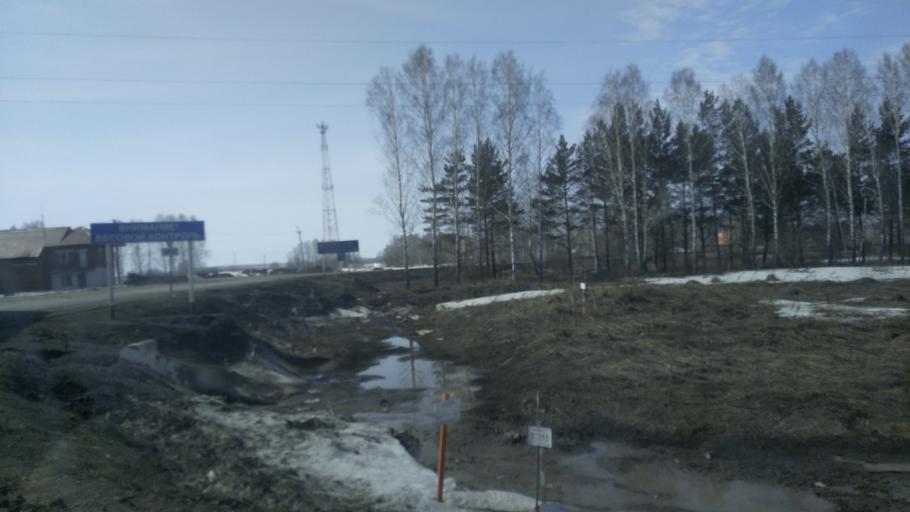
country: RU
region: Kemerovo
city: Yurga
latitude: 55.6244
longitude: 84.8198
